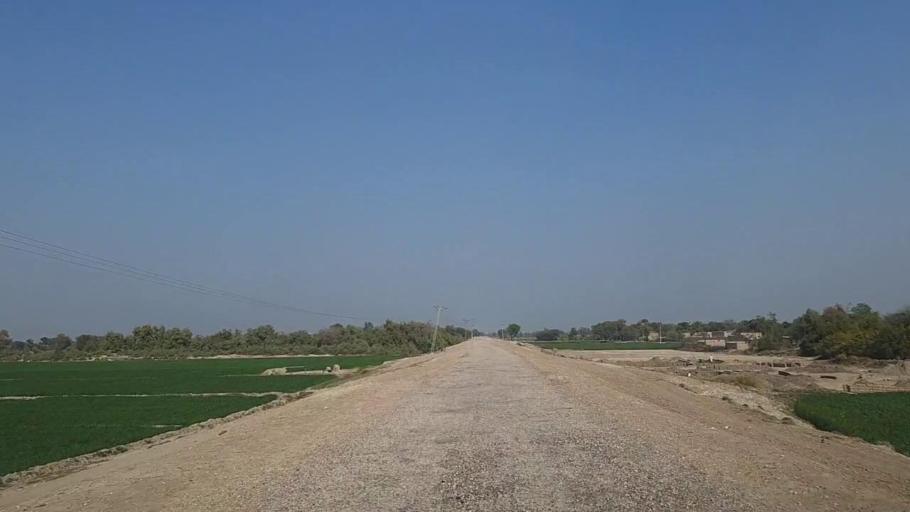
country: PK
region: Sindh
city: Moro
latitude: 26.8008
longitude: 67.9450
